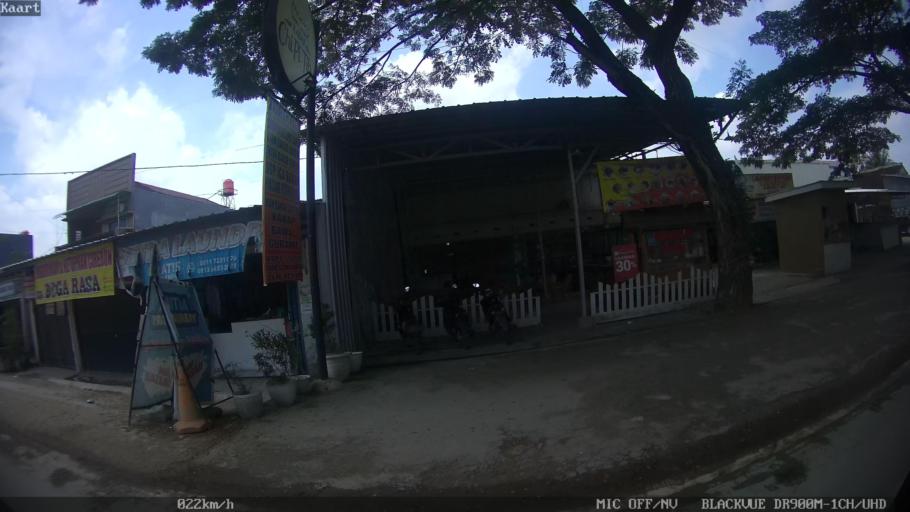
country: ID
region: Lampung
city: Kedaton
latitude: -5.3614
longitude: 105.3042
